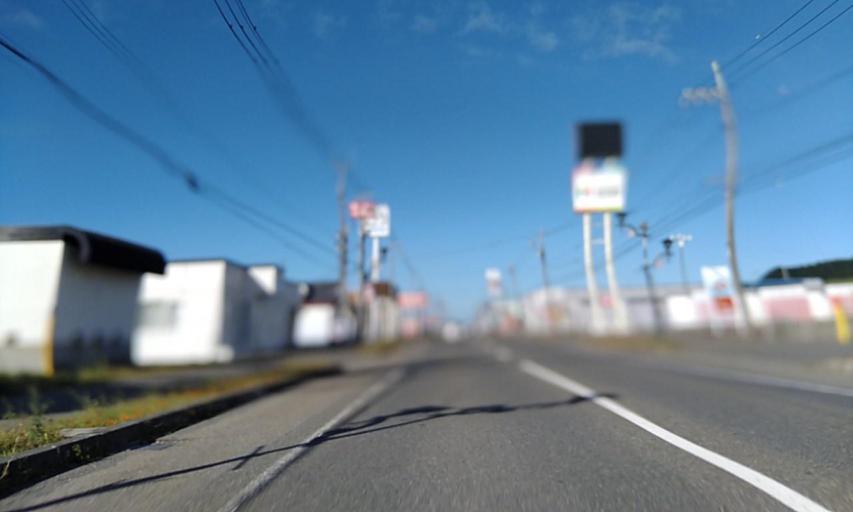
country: JP
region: Hokkaido
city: Shizunai-furukawacho
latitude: 42.3416
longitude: 142.3521
